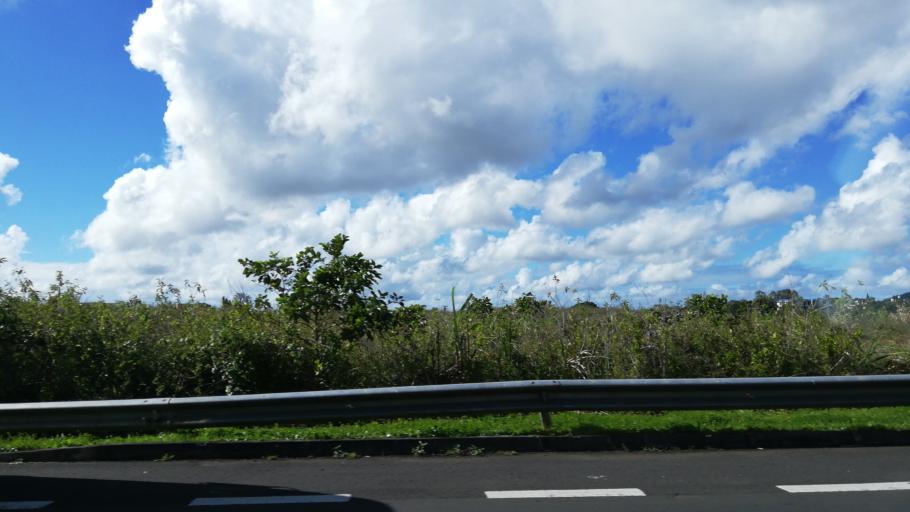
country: MU
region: Moka
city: Quartier Militaire
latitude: -20.2473
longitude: 57.5888
